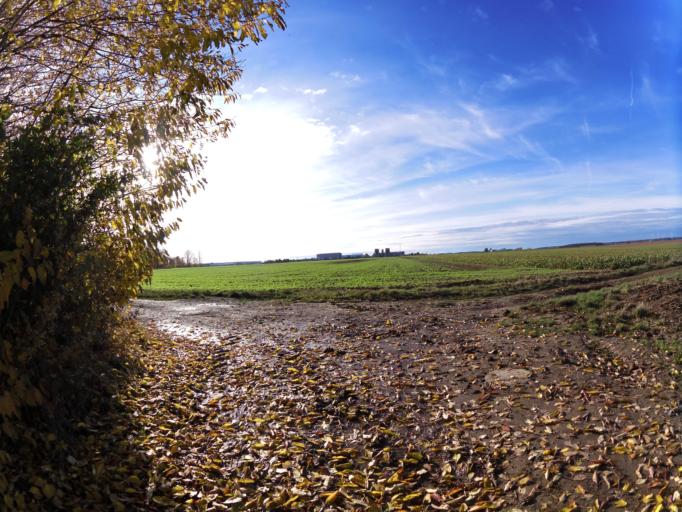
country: DE
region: Bavaria
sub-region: Regierungsbezirk Unterfranken
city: Giebelstadt
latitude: 49.6572
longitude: 9.9673
